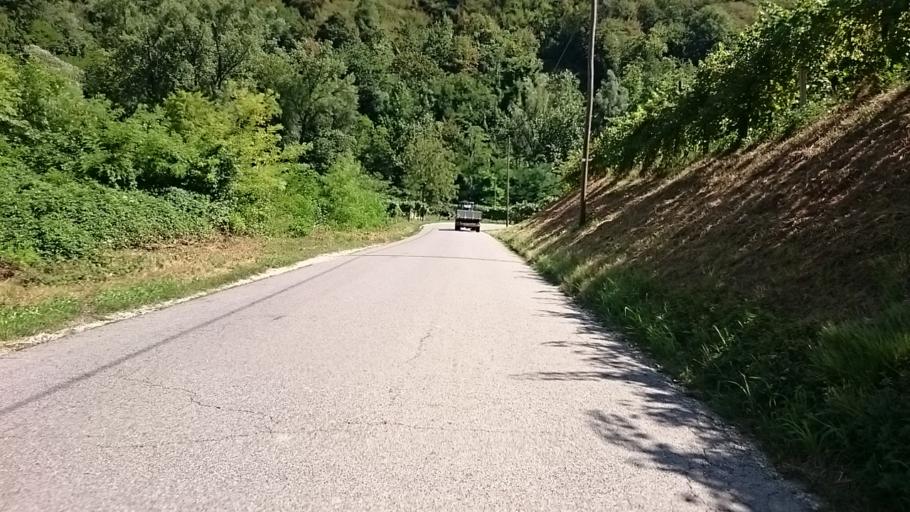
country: IT
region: Veneto
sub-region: Provincia di Treviso
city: Miane
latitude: 45.9126
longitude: 12.0773
